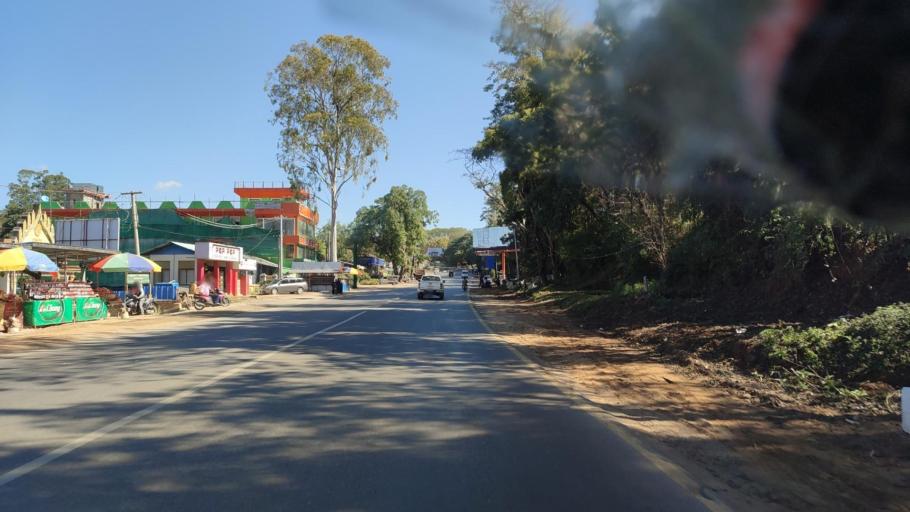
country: MM
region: Mandalay
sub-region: Pyin Oo Lwin District
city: Pyin Oo Lwin
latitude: 22.0114
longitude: 96.4407
